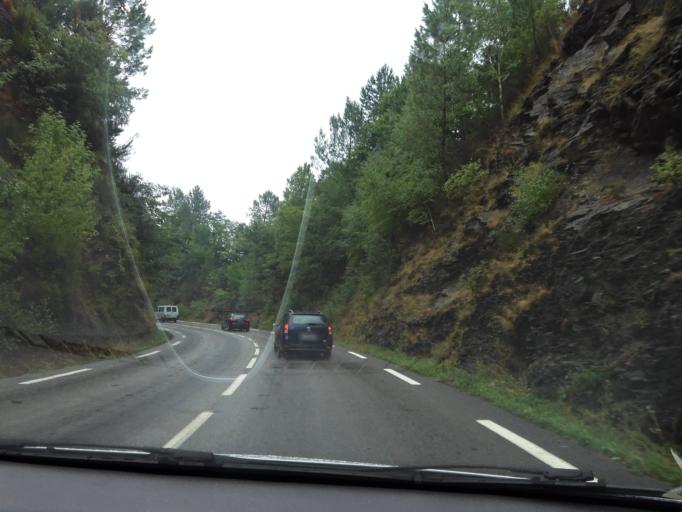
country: FR
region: Languedoc-Roussillon
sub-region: Departement du Gard
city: Branoux-les-Taillades
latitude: 44.2502
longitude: 3.9572
